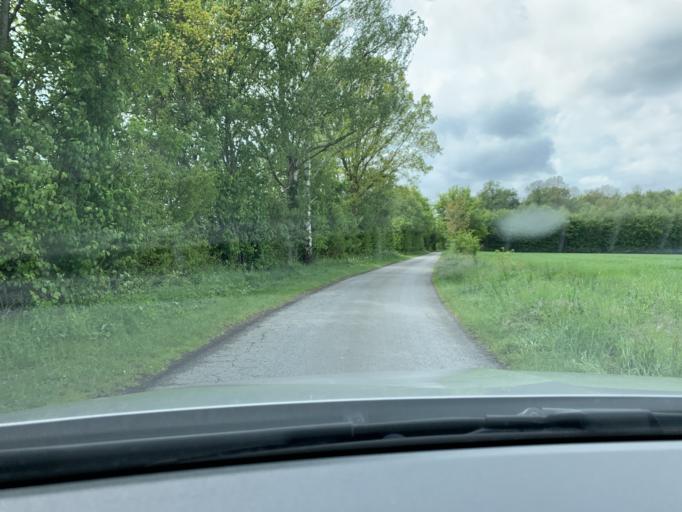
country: DE
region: North Rhine-Westphalia
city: Rietberg
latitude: 51.7935
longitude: 8.3832
